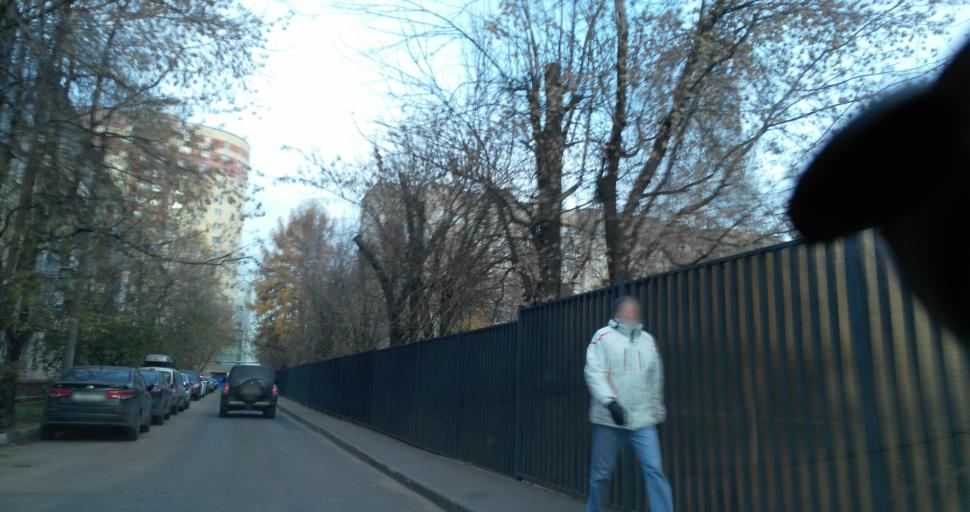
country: RU
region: Moscow
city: Khimki
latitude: 55.8931
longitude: 37.4344
